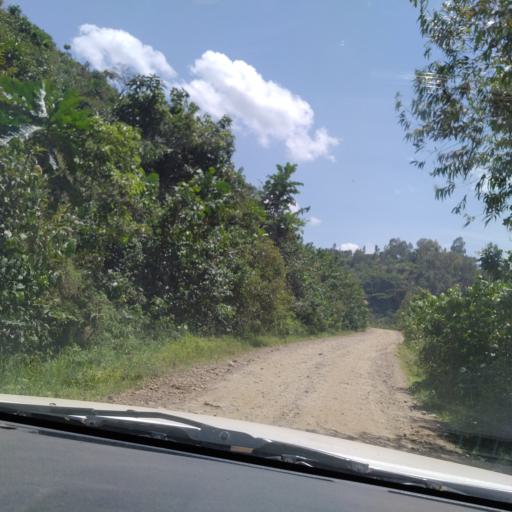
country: CD
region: Nord Kivu
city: Sake
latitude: -1.9692
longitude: 28.9147
